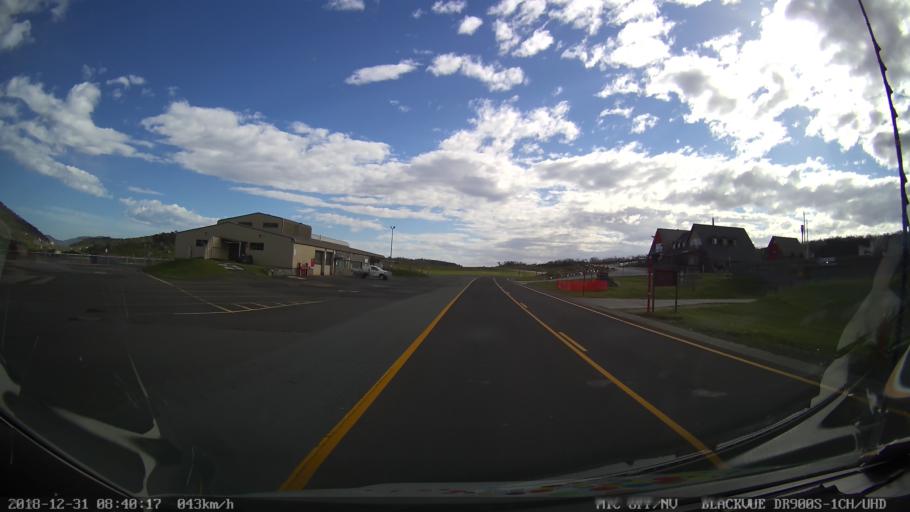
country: AU
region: New South Wales
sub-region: Snowy River
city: Jindabyne
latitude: -36.4055
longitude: 148.4123
